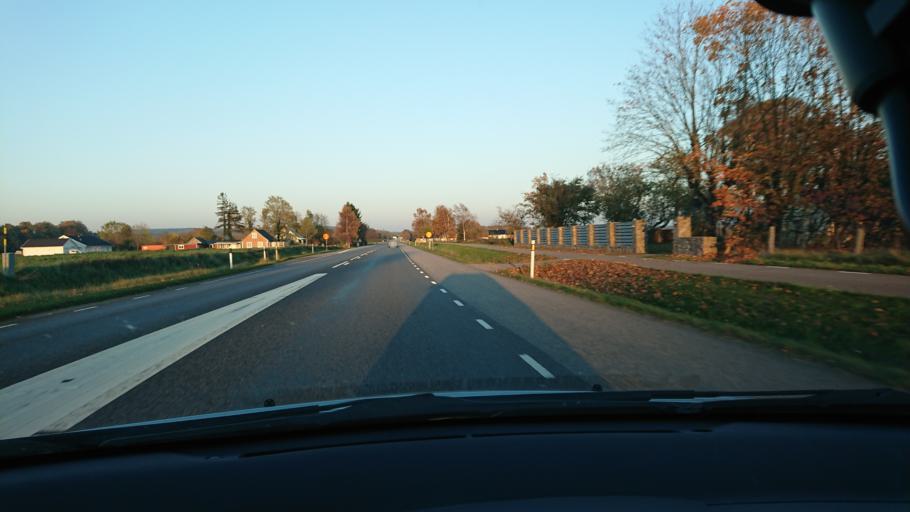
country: SE
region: Halland
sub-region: Halmstads Kommun
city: Fyllinge
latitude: 56.6858
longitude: 12.9489
